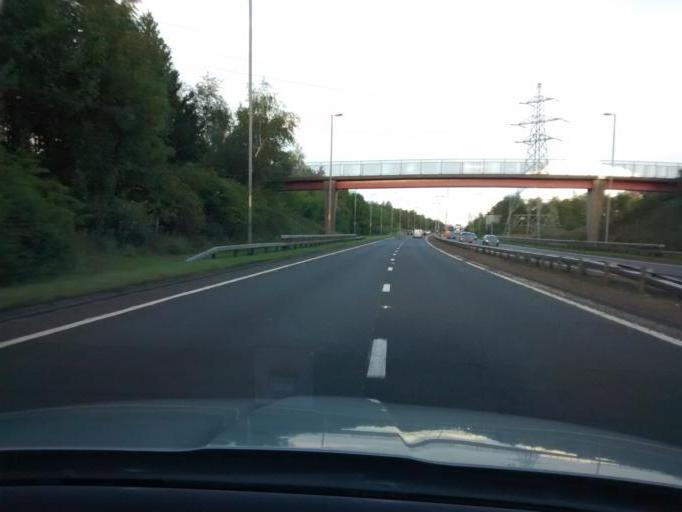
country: GB
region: Scotland
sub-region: Renfrewshire
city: Elderslie
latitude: 55.8434
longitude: -4.5003
